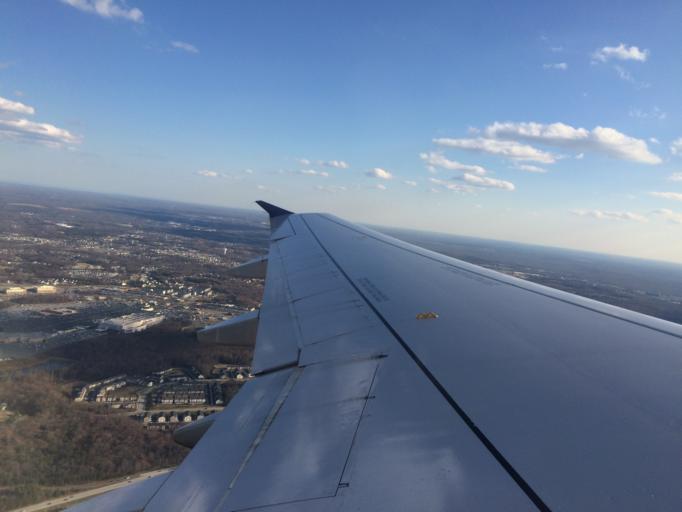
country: US
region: Maryland
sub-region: Howard County
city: Hanover
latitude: 39.1761
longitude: -76.7373
